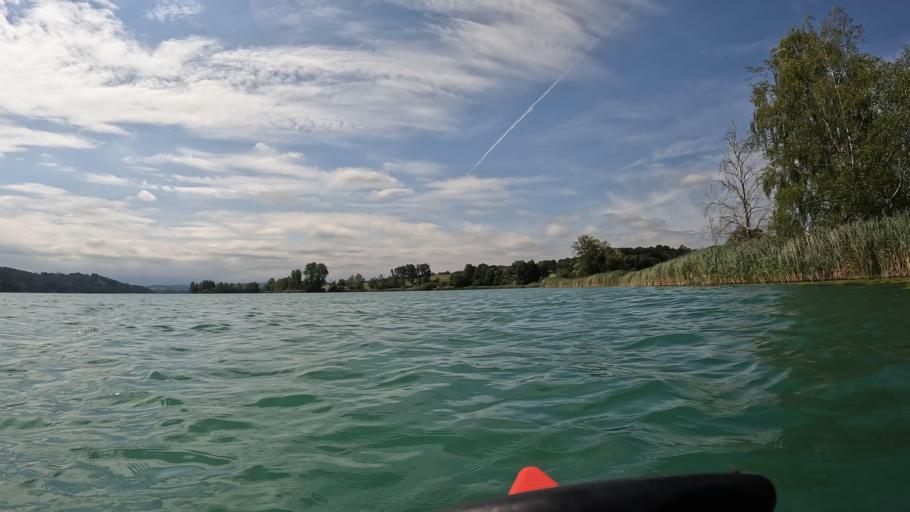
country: DE
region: Bavaria
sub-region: Upper Bavaria
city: Taching am See
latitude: 47.9853
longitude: 12.7413
